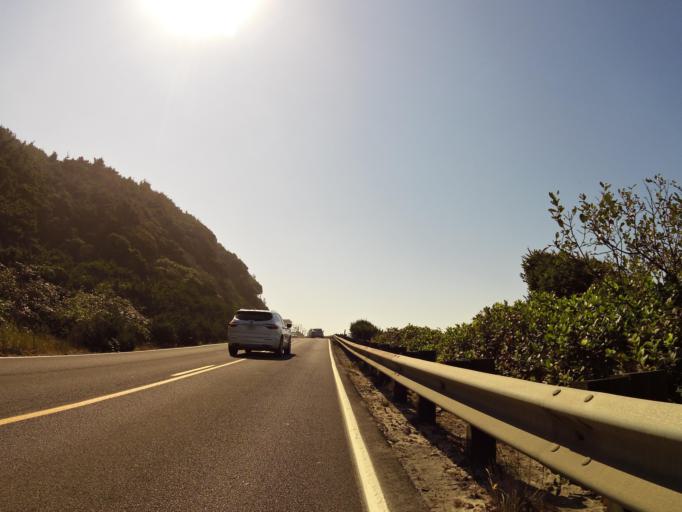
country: US
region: Oregon
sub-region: Tillamook County
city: Pacific City
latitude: 45.2413
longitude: -123.9689
